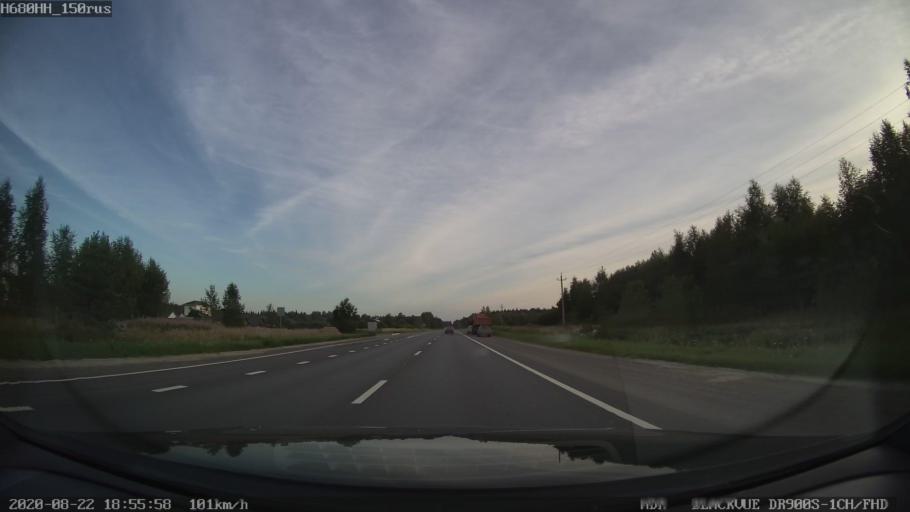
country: RU
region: Tverskaya
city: Rameshki
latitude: 57.1908
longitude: 36.0839
